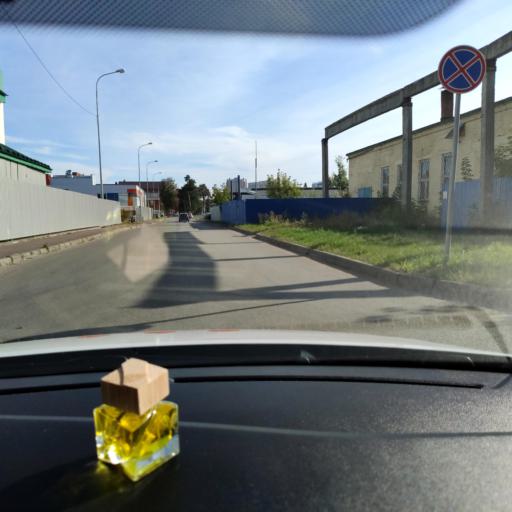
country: RU
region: Tatarstan
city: Staroye Arakchino
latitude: 55.8364
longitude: 49.0494
